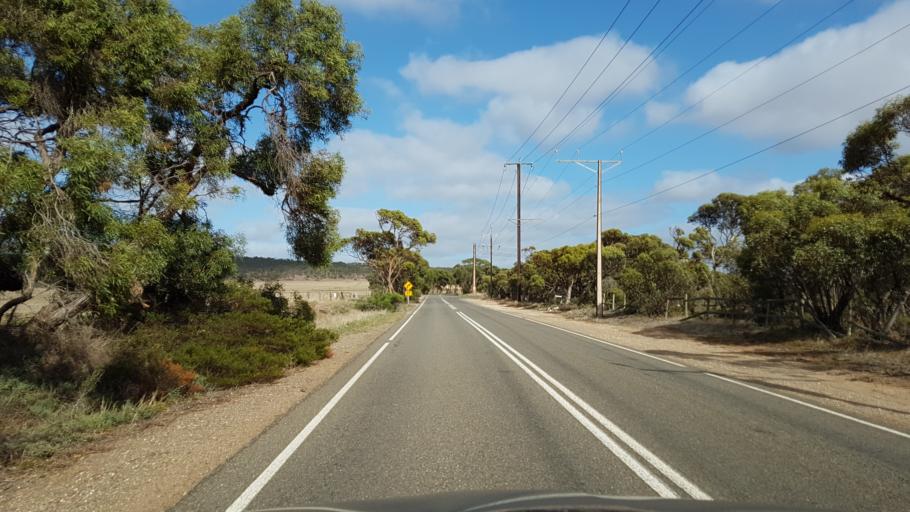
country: AU
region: South Australia
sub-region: Murray Bridge
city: Murray Bridge
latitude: -35.1178
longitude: 139.2387
